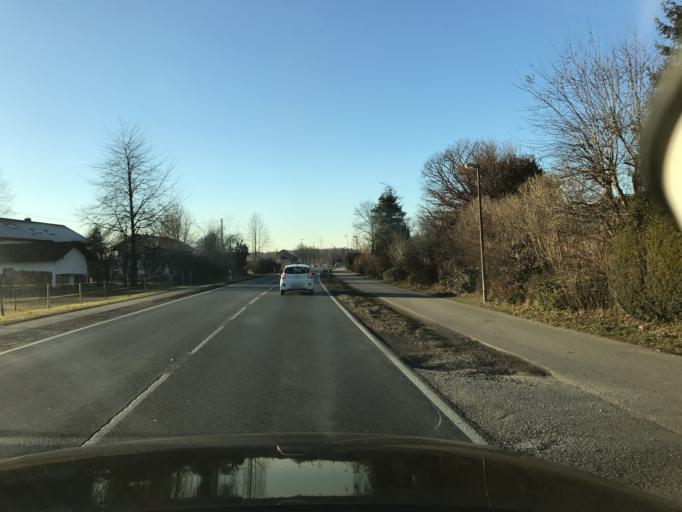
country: DE
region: Bavaria
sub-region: Upper Bavaria
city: Kolbermoor
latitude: 47.8418
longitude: 12.0380
